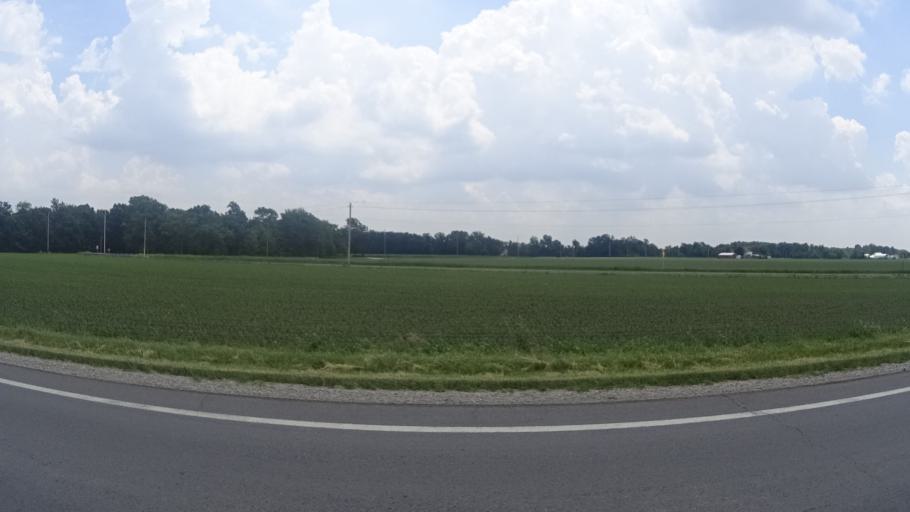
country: US
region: Ohio
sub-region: Huron County
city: Monroeville
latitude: 41.2877
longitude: -82.6785
